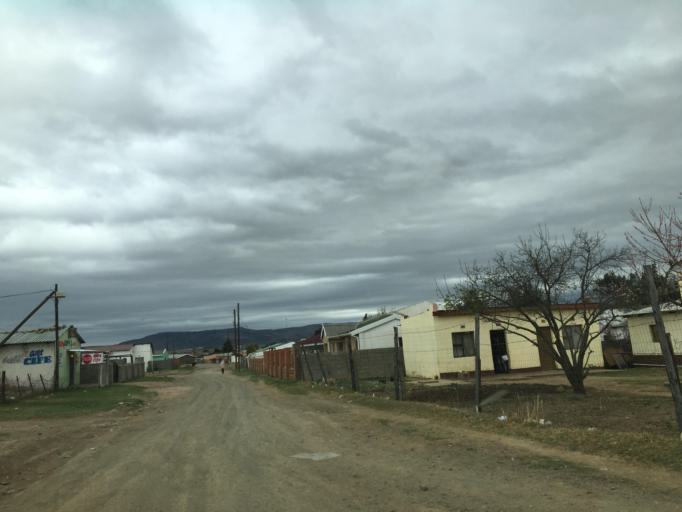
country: ZA
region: Eastern Cape
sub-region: Chris Hani District Municipality
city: Cala
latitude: -31.5294
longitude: 27.6980
